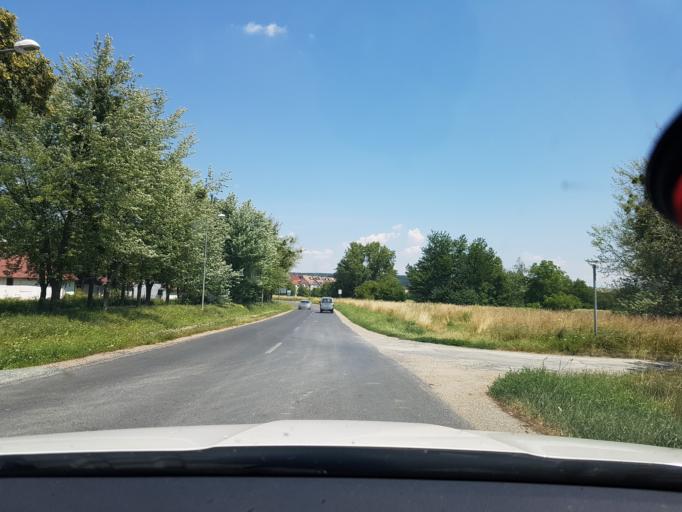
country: HU
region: Vas
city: Koszeg
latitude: 47.3778
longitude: 16.5439
